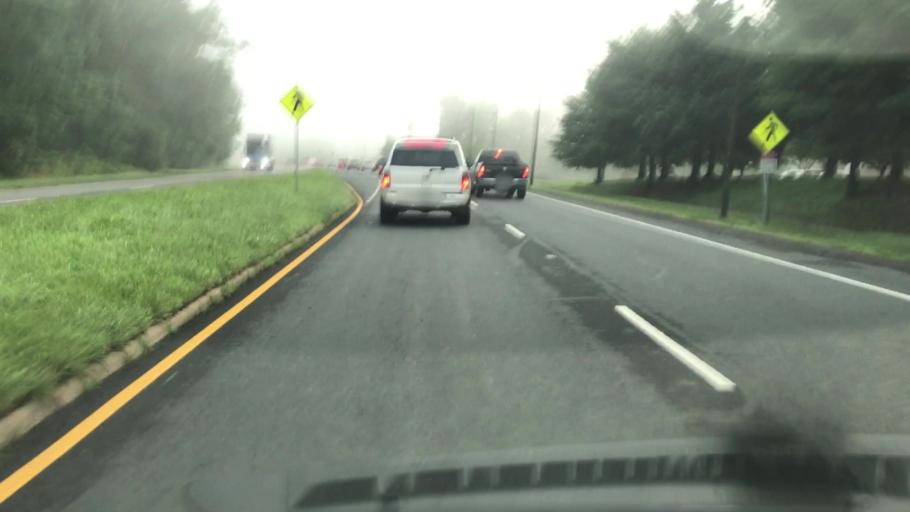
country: US
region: Virginia
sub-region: Fairfax County
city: Fairfax Station
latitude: 38.8224
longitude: -77.3176
